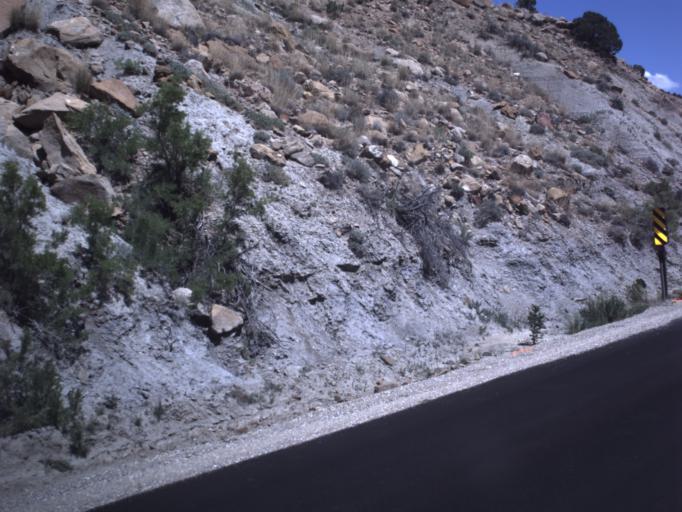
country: US
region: Utah
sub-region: Emery County
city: Orangeville
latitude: 39.2704
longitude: -111.1544
